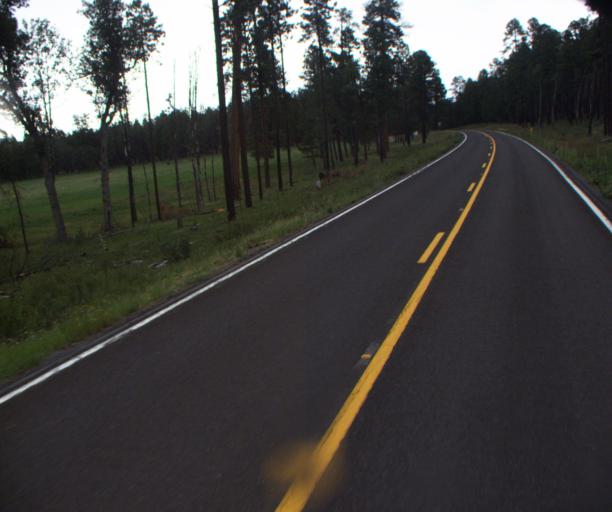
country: US
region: Arizona
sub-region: Apache County
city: Eagar
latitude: 33.6857
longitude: -109.2257
